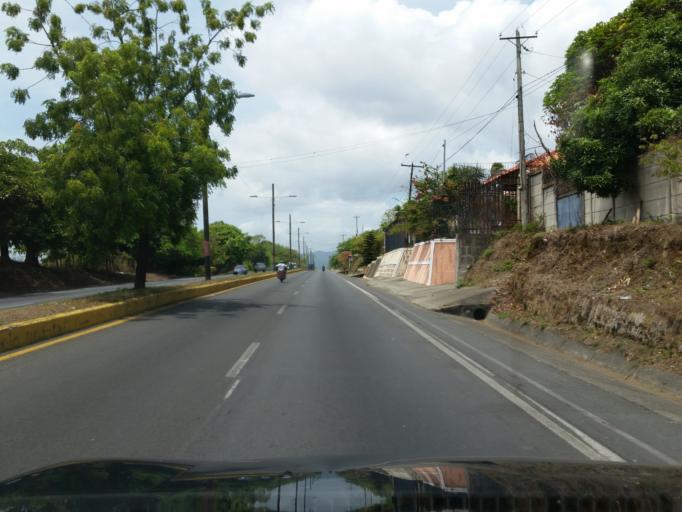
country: NI
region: Masaya
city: Nindiri
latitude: 12.0109
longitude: -86.1400
